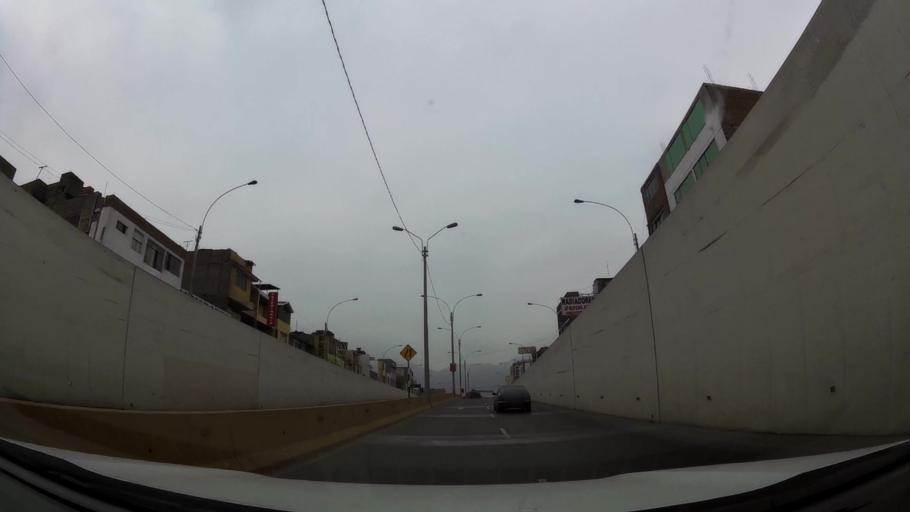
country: PE
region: Lima
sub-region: Lima
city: Independencia
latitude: -11.9835
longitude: -77.0639
